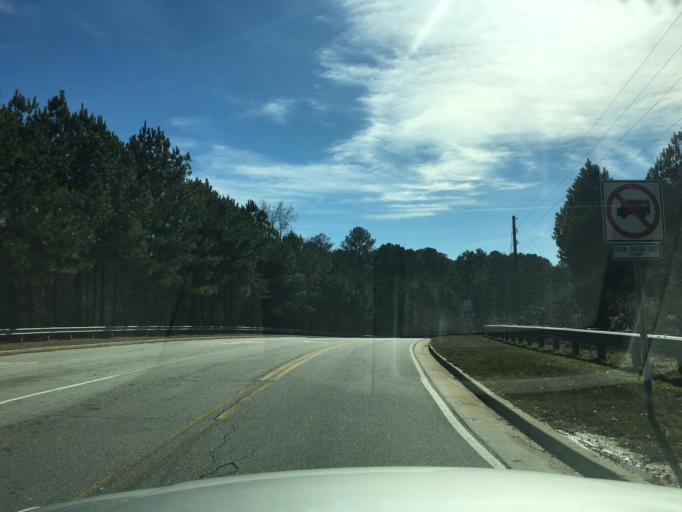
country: US
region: Georgia
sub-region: Rockdale County
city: Lakeview Estates
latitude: 33.7729
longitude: -84.0507
